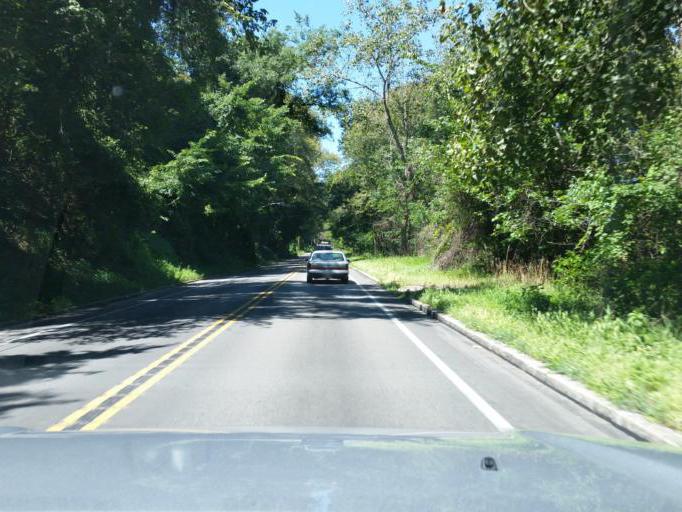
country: US
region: Pennsylvania
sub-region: Allegheny County
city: Aspinwall
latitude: 40.4824
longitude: -79.8919
